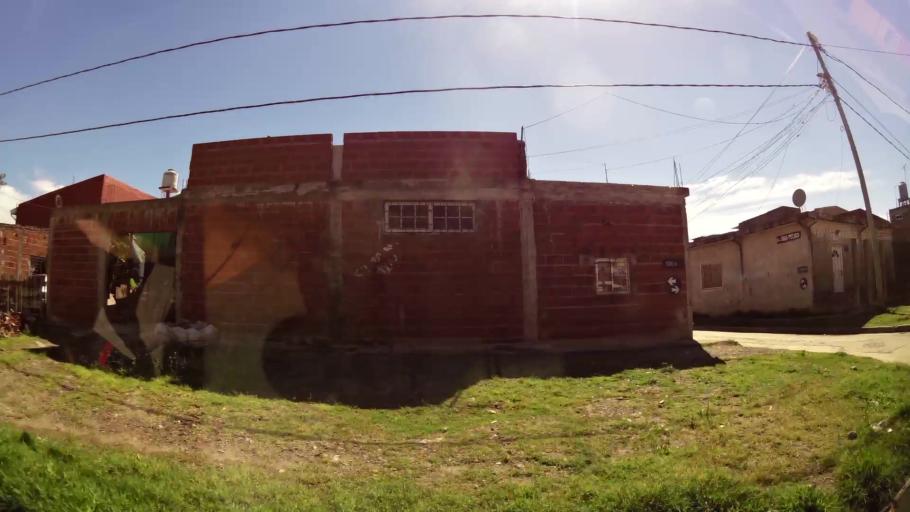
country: AR
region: Buenos Aires
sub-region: Partido de Quilmes
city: Quilmes
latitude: -34.6874
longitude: -58.3028
